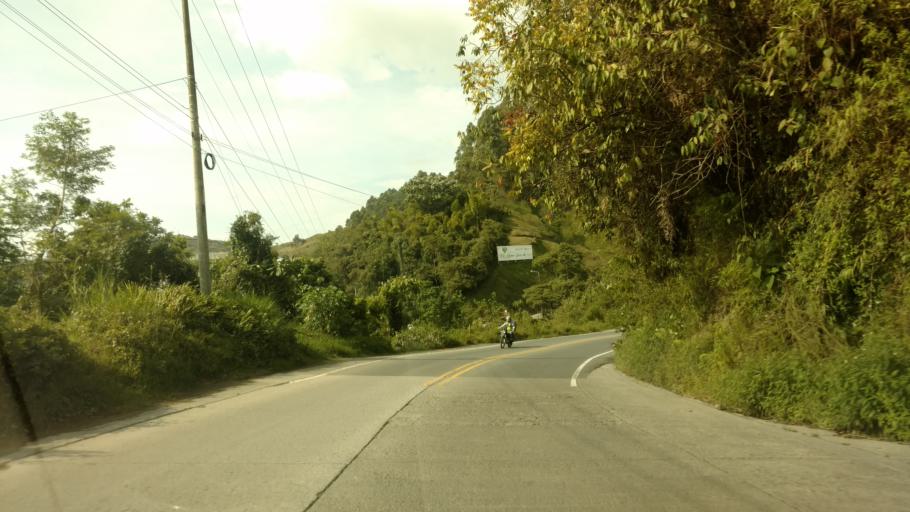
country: CO
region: Caldas
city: Manizales
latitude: 5.0773
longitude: -75.5106
